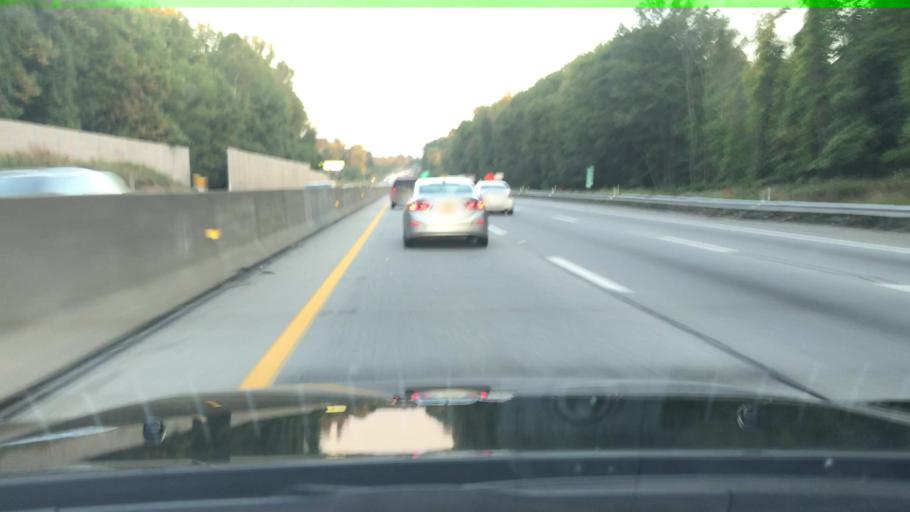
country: US
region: Pennsylvania
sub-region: Bucks County
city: Feasterville
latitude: 40.1494
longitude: -75.0191
